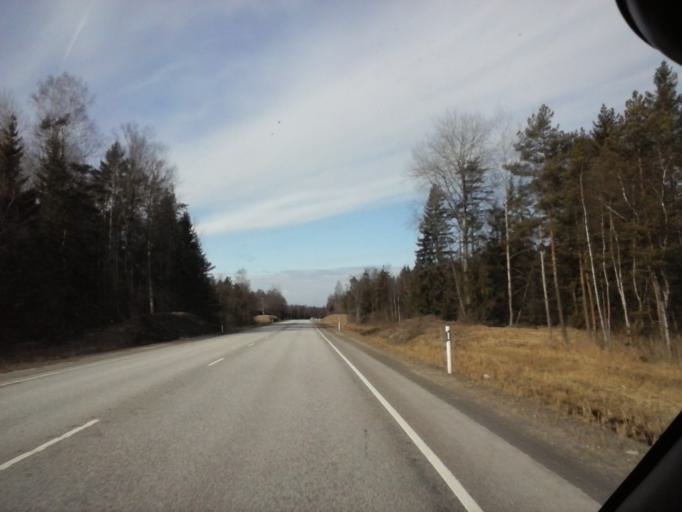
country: EE
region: Jaervamaa
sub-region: Paide linn
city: Paide
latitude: 59.0318
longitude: 25.5025
